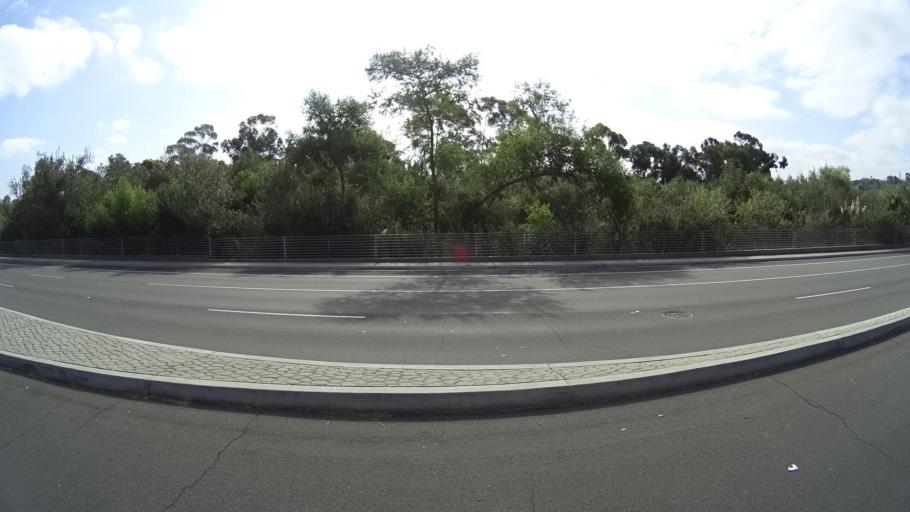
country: US
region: California
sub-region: San Diego County
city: Encinitas
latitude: 33.0698
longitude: -117.2454
